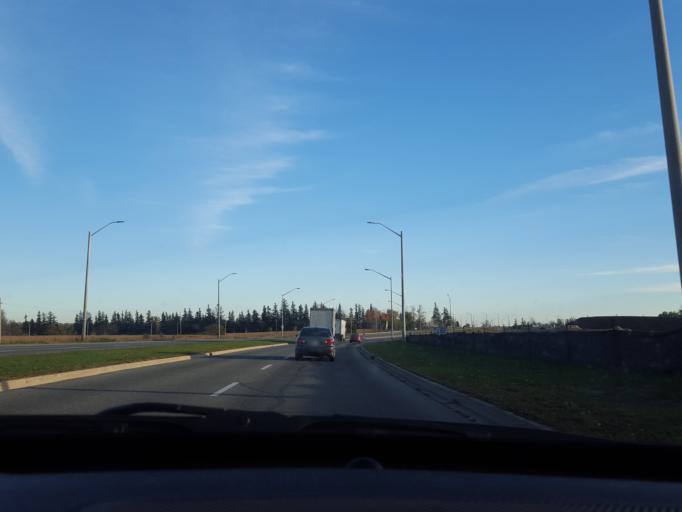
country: CA
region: Ontario
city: Markham
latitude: 43.8992
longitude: -79.2158
